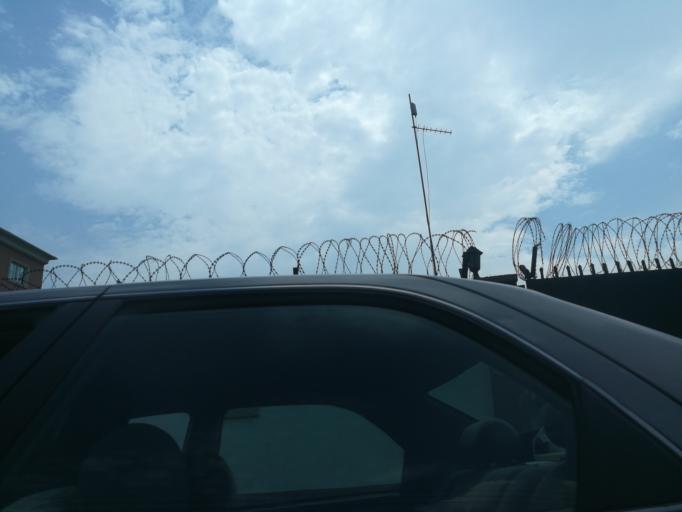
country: NG
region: Lagos
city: Ikeja
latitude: 6.6036
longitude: 3.3652
